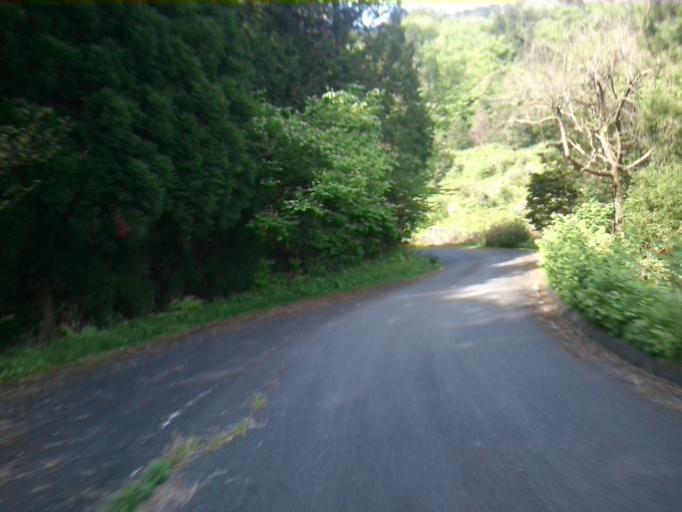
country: JP
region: Kyoto
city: Miyazu
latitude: 35.6646
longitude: 135.2332
